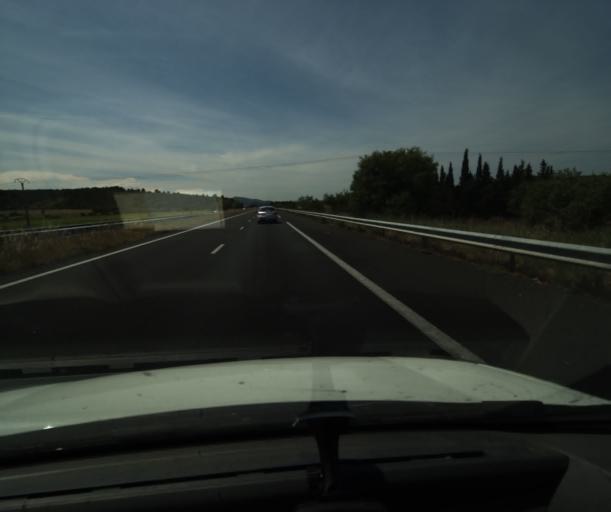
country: FR
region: Languedoc-Roussillon
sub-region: Departement de l'Aude
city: Lezignan-Corbieres
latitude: 43.1705
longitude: 2.7709
